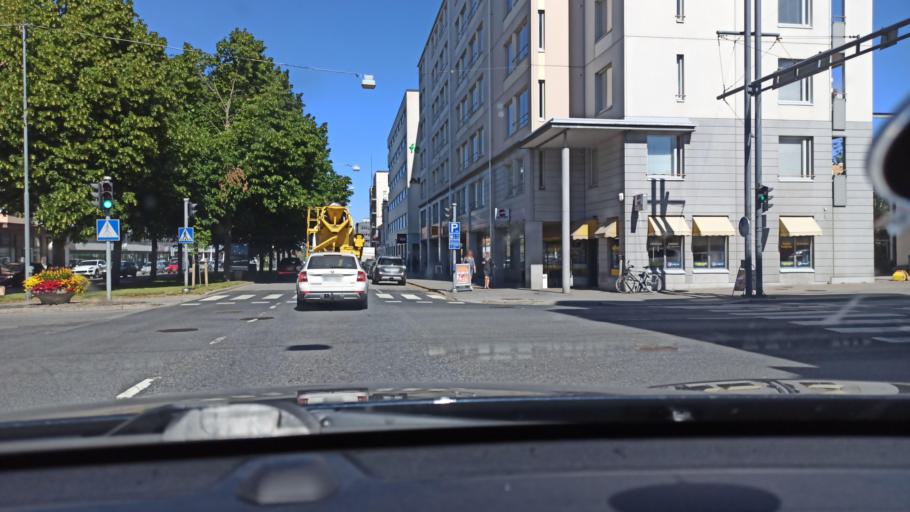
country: FI
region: Ostrobothnia
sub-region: Vaasa
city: Vaasa
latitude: 63.0935
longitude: 21.6182
